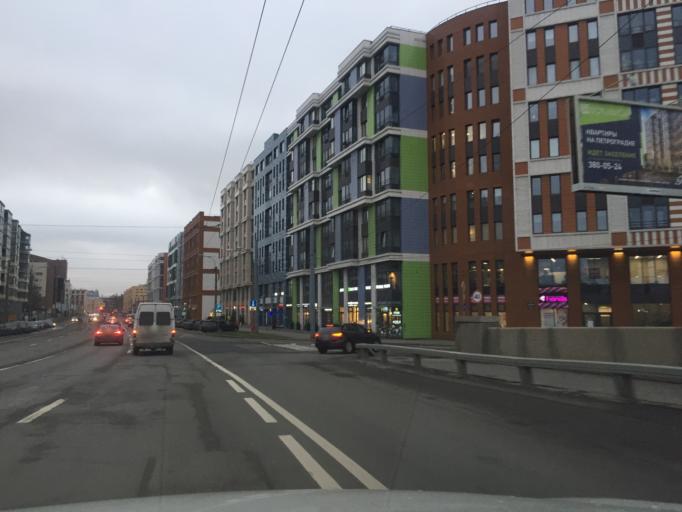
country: RU
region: St.-Petersburg
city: Petrogradka
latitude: 59.9764
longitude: 30.3181
